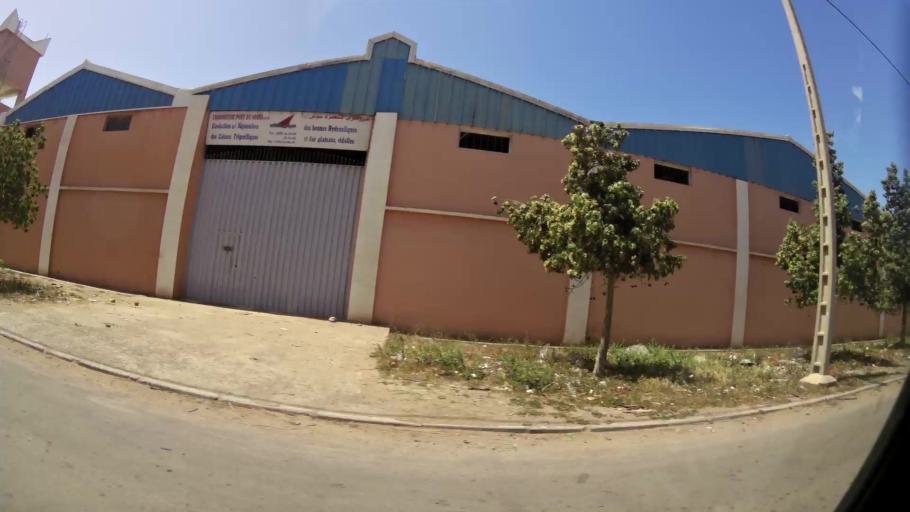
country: MA
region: Souss-Massa-Draa
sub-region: Inezgane-Ait Mellou
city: Inezgane
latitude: 30.3362
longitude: -9.4875
